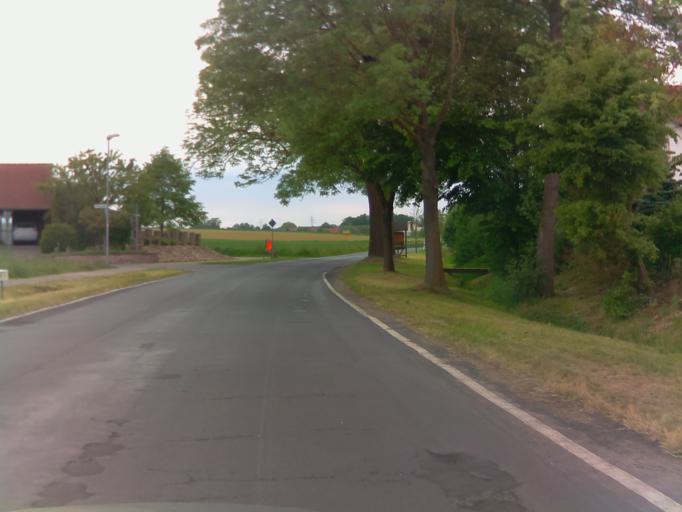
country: DE
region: Hesse
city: Schwalmstadt
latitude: 50.8853
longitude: 9.2452
